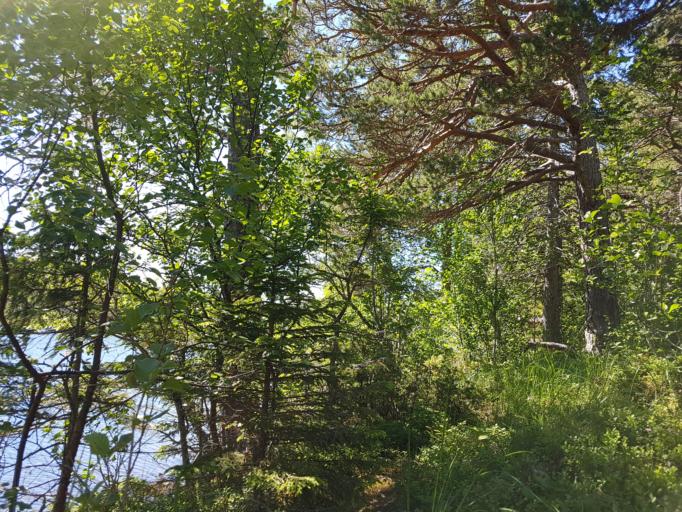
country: NO
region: Sor-Trondelag
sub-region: Melhus
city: Melhus
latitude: 63.4383
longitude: 10.2150
